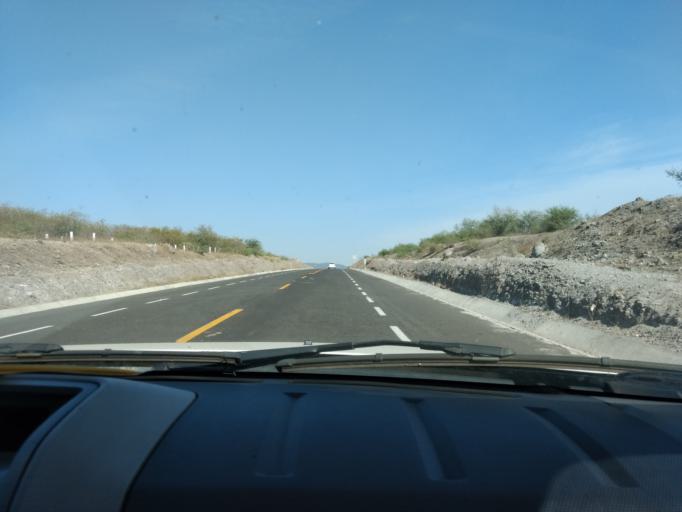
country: MX
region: Morelos
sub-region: Ayala
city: El Salitre
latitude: 18.6677
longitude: -98.9638
